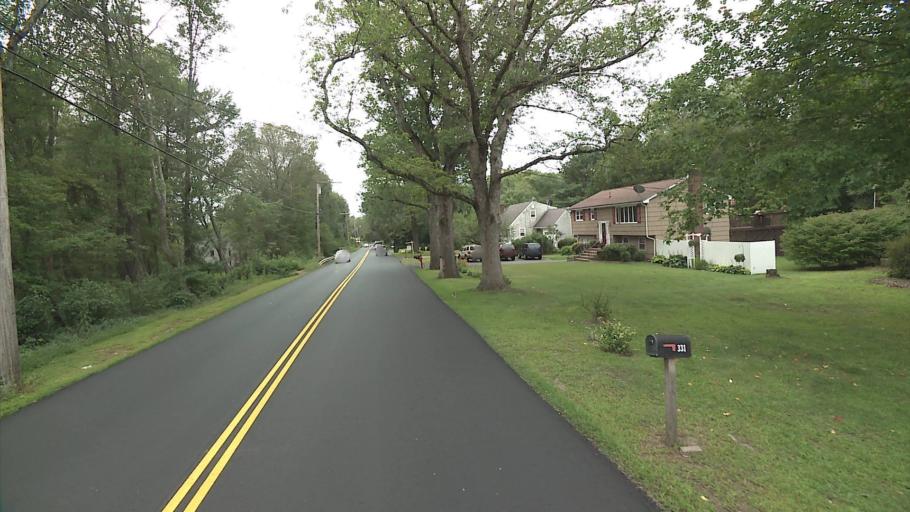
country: US
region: Connecticut
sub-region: New London County
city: Colchester
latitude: 41.5873
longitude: -72.3378
